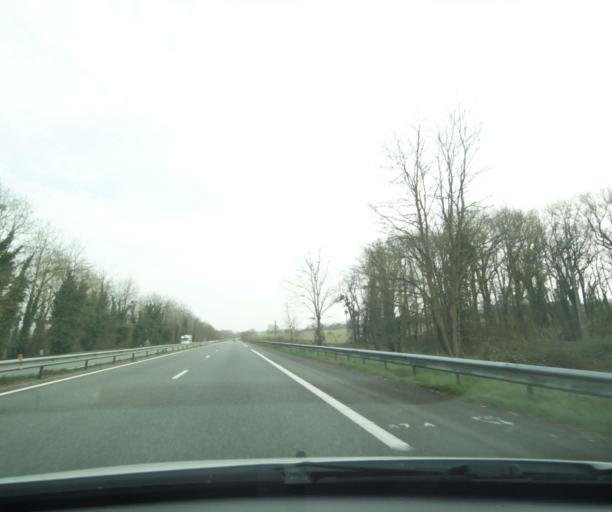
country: FR
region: Aquitaine
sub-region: Departement des Pyrenees-Atlantiques
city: Orthez
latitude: 43.5056
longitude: -0.8387
